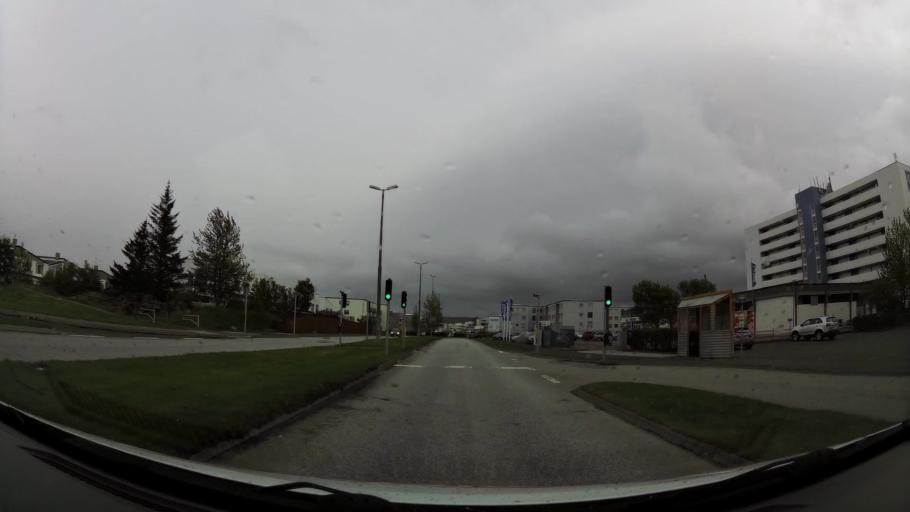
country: IS
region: Capital Region
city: Hafnarfjoerdur
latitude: 64.0794
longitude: -21.9584
